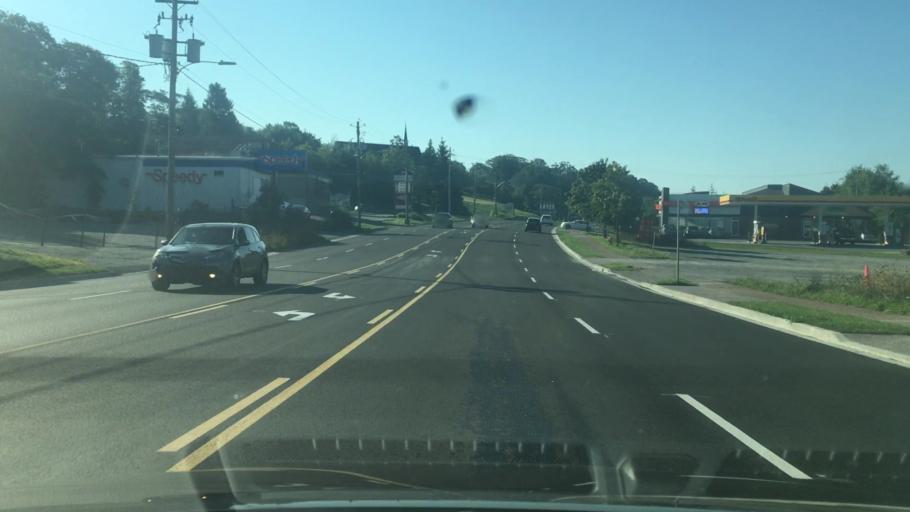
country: CA
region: Nova Scotia
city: Dartmouth
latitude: 44.7405
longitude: -63.6549
